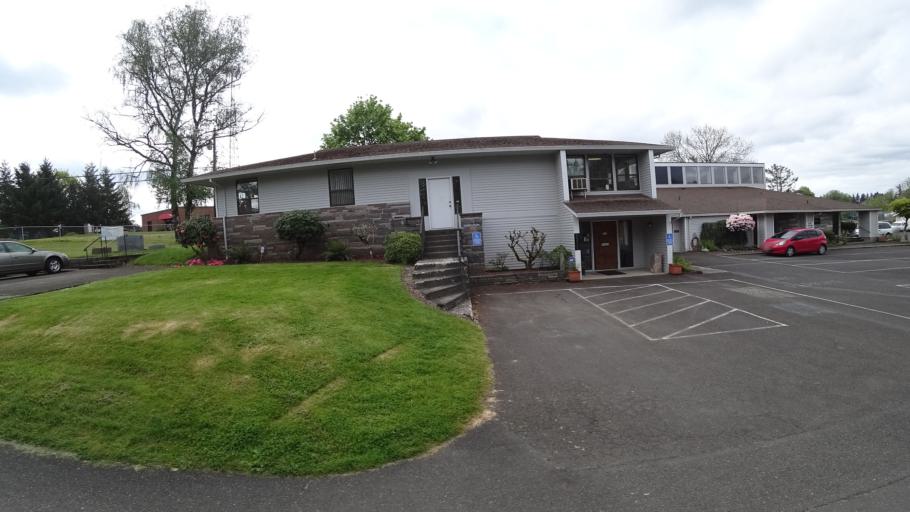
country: US
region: Oregon
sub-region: Washington County
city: Hillsboro
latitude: 45.5228
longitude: -123.0017
